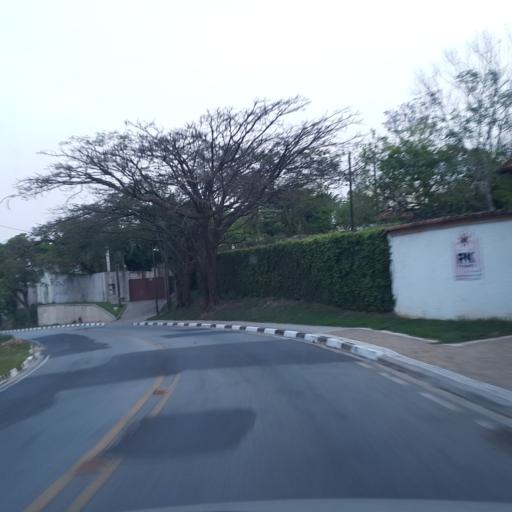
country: BR
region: Sao Paulo
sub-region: Vinhedo
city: Vinhedo
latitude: -23.0537
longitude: -46.9774
